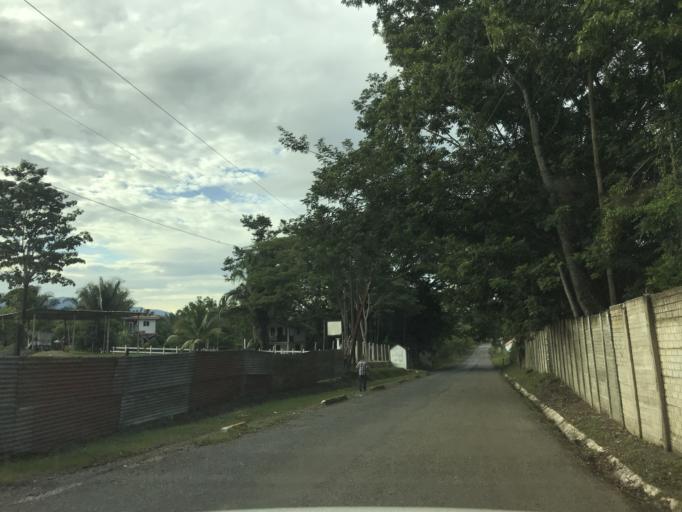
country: GT
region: Izabal
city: Morales
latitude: 15.6349
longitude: -89.0063
